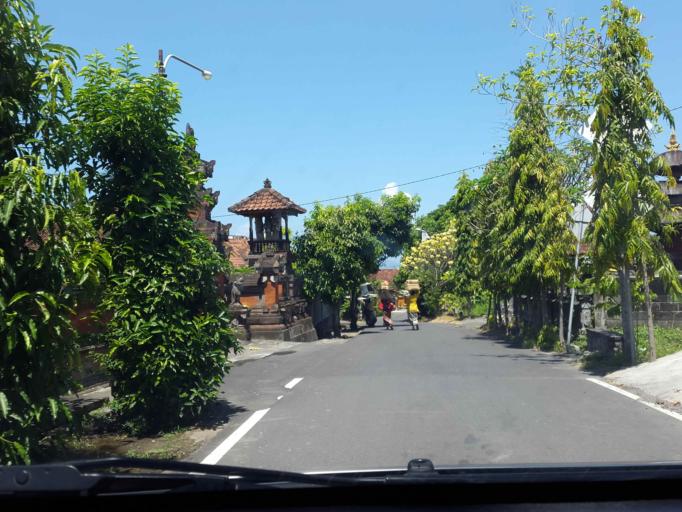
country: ID
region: Bali
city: Dawan
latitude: -8.5618
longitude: 115.4207
